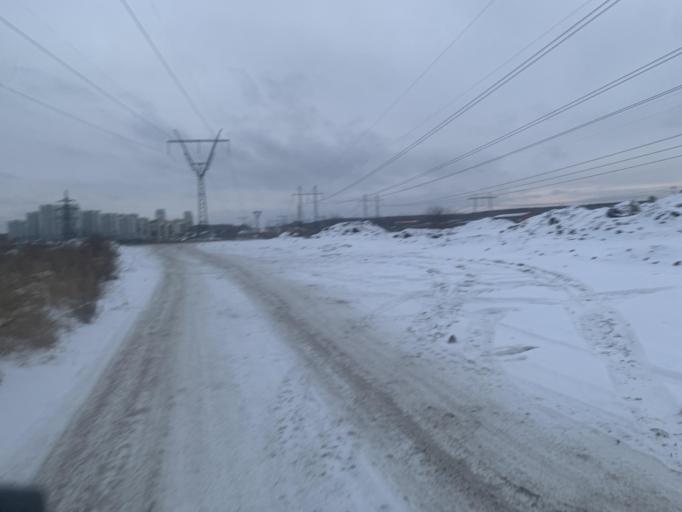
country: RU
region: Chelyabinsk
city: Roshchino
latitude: 55.1853
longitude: 61.2573
